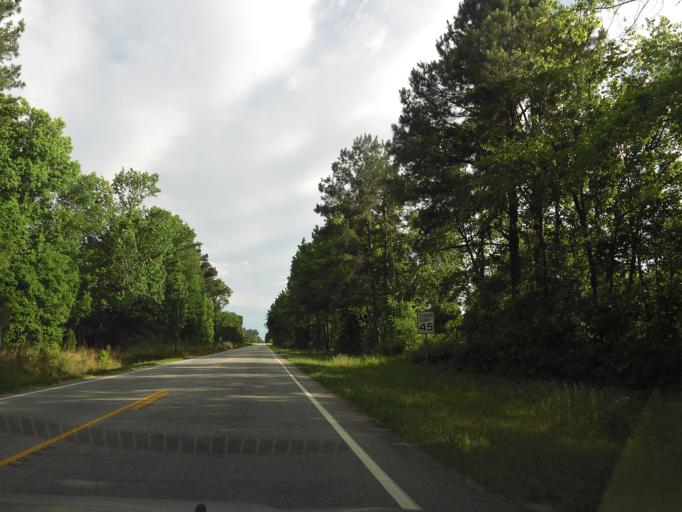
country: US
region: South Carolina
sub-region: Hampton County
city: Estill
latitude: 32.6780
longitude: -81.2432
